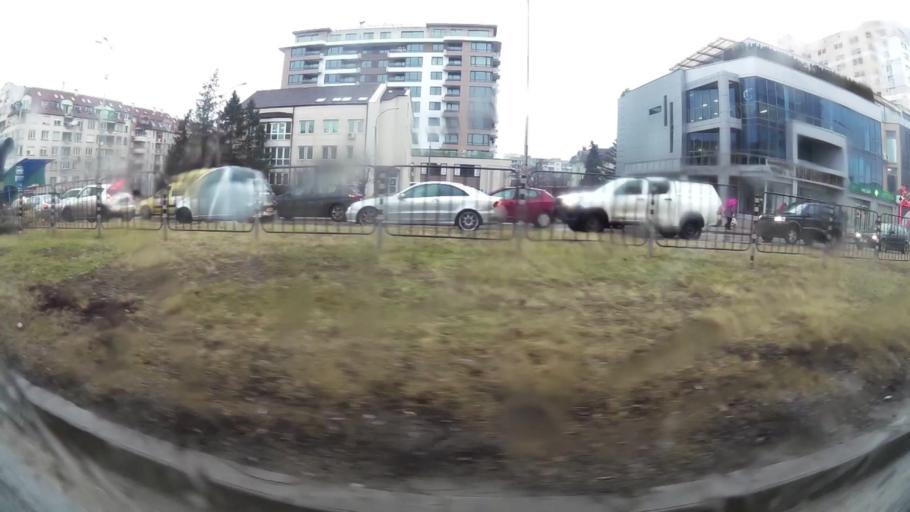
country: BG
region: Sofia-Capital
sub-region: Stolichna Obshtina
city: Sofia
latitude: 42.6534
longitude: 23.3724
